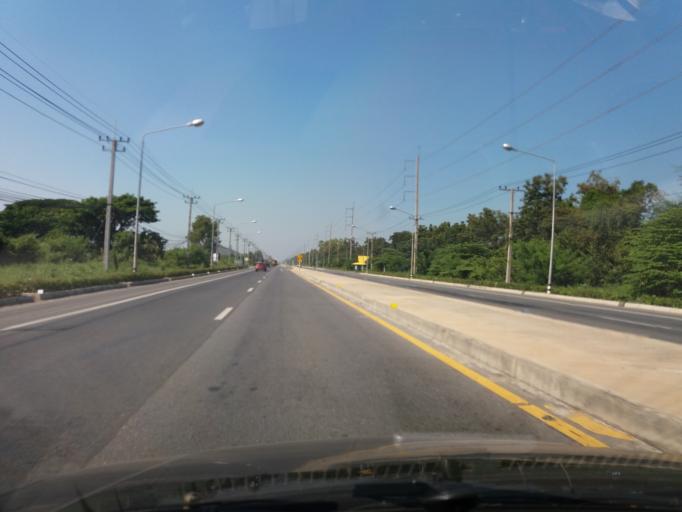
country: TH
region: Chai Nat
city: Chai Nat
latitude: 15.2259
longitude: 100.1107
